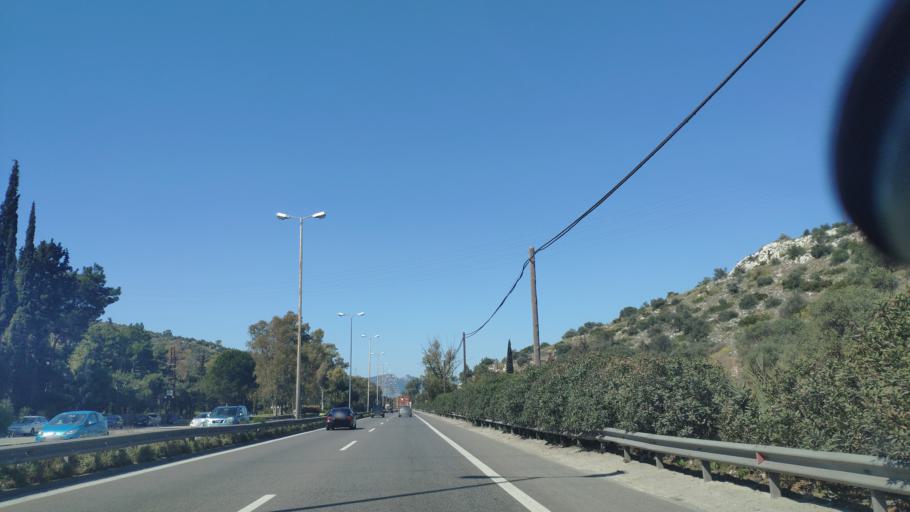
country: GR
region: Attica
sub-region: Nomarchia Athinas
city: Skaramangas
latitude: 38.0130
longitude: 23.6208
